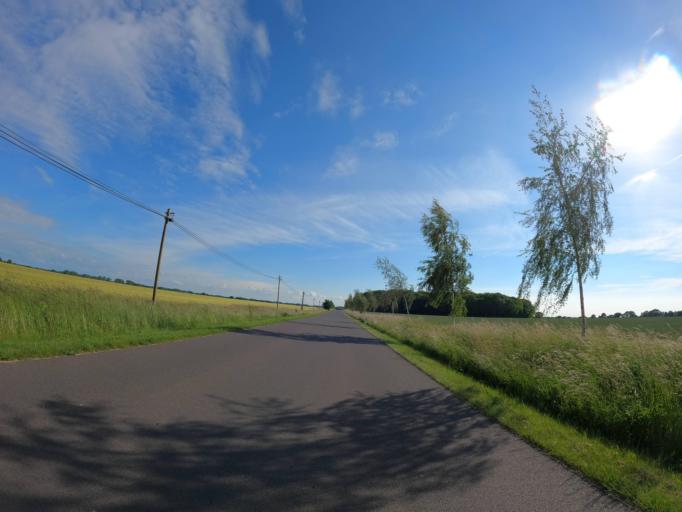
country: DE
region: Mecklenburg-Vorpommern
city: Preetz
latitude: 54.3486
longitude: 12.9880
